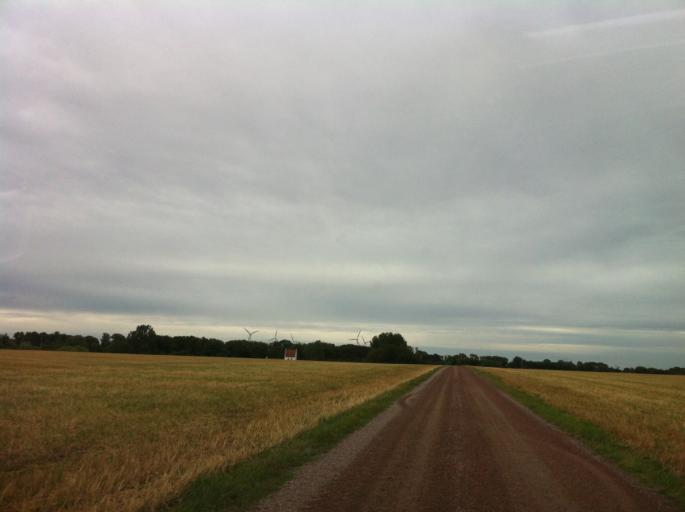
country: SE
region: Skane
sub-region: Landskrona
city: Asmundtorp
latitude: 55.9329
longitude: 12.9925
